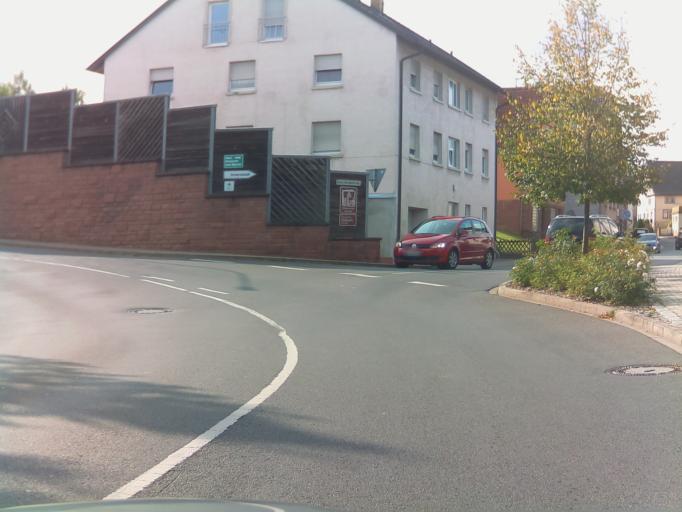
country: DE
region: Baden-Wuerttemberg
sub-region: Karlsruhe Region
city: Walldurn
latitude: 49.5807
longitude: 9.3725
